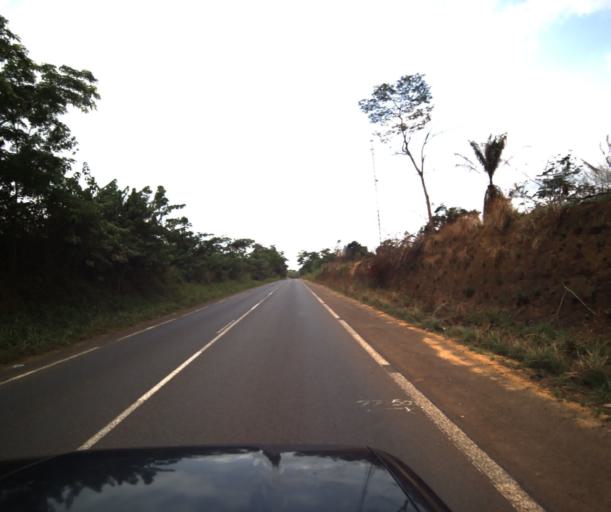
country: CM
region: Centre
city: Eseka
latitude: 3.8717
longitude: 10.9007
